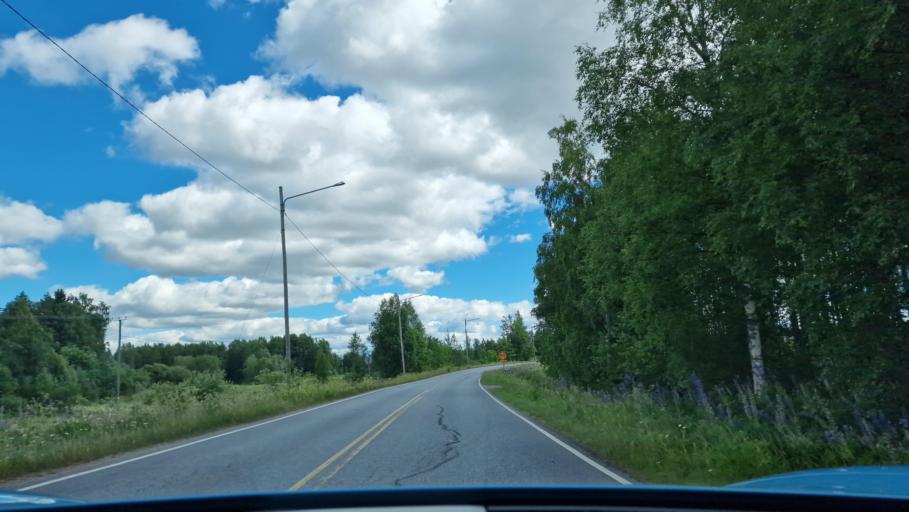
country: FI
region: Southern Ostrobothnia
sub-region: Jaerviseutu
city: Soini
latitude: 62.8446
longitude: 24.3237
